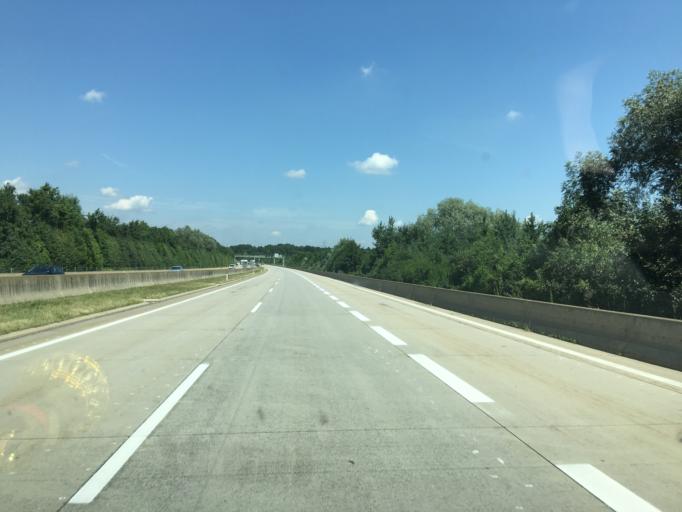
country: AT
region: Styria
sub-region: Politischer Bezirk Leibnitz
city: Spielfeld
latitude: 46.7091
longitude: 15.6425
